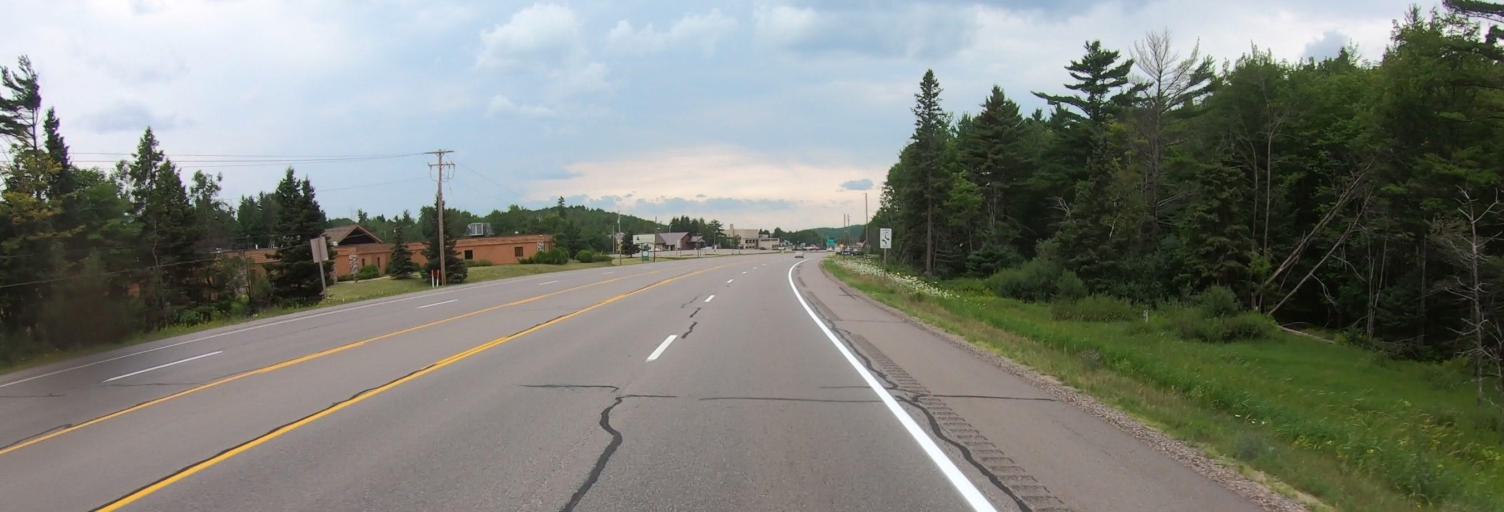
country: US
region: Michigan
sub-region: Marquette County
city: Ishpeming
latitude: 46.5080
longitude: -87.6479
